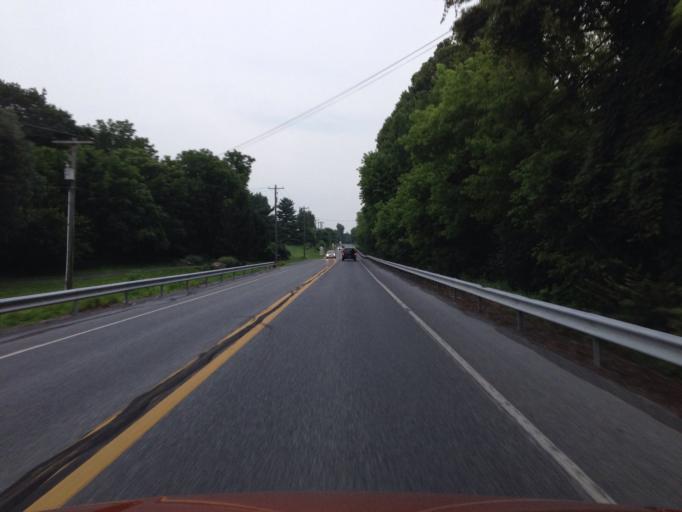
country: US
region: Pennsylvania
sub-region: Lancaster County
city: Rothsville
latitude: 40.1591
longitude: -76.2289
